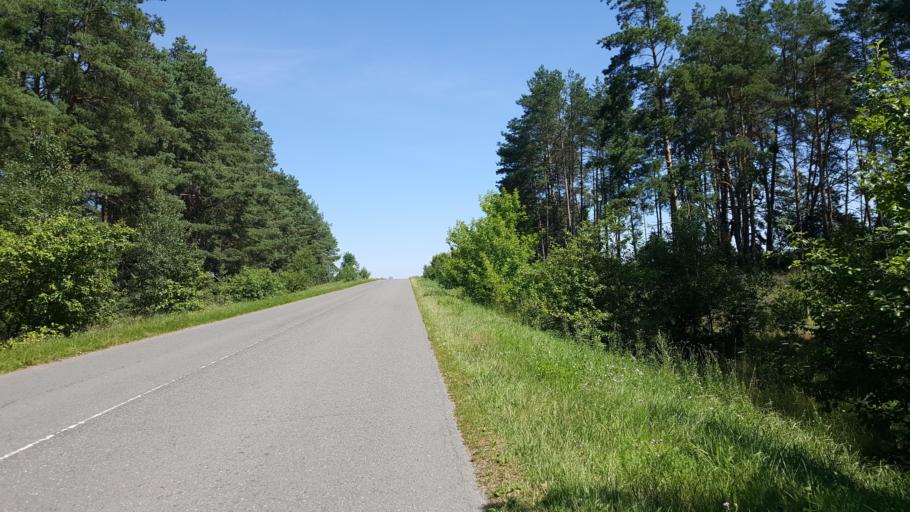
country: BY
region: Brest
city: Pruzhany
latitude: 52.5338
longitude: 24.1942
